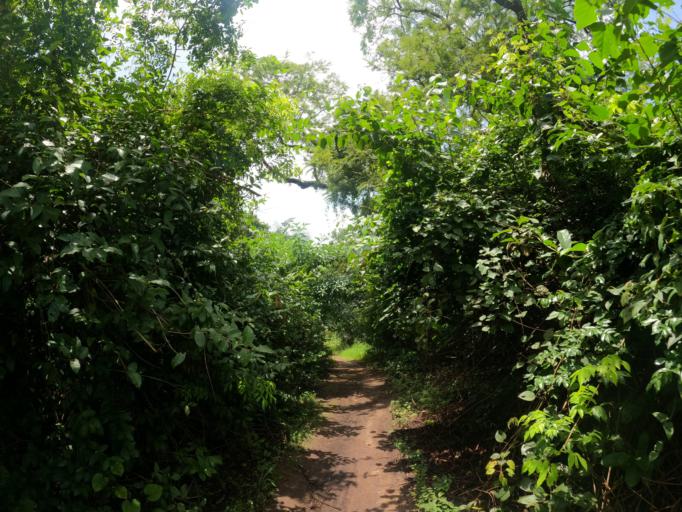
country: SL
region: Northern Province
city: Binkolo
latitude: 9.1482
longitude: -12.2493
